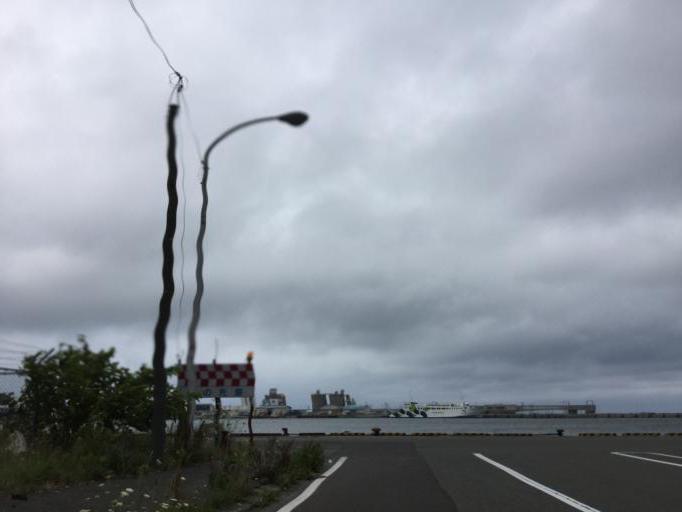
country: JP
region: Hokkaido
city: Wakkanai
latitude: 45.4096
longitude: 141.6821
